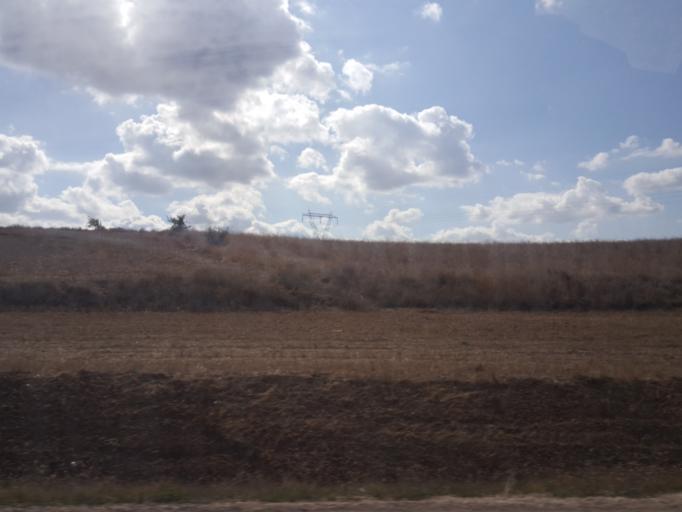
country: TR
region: Tokat
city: Camlibel
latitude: 40.1991
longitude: 36.4841
